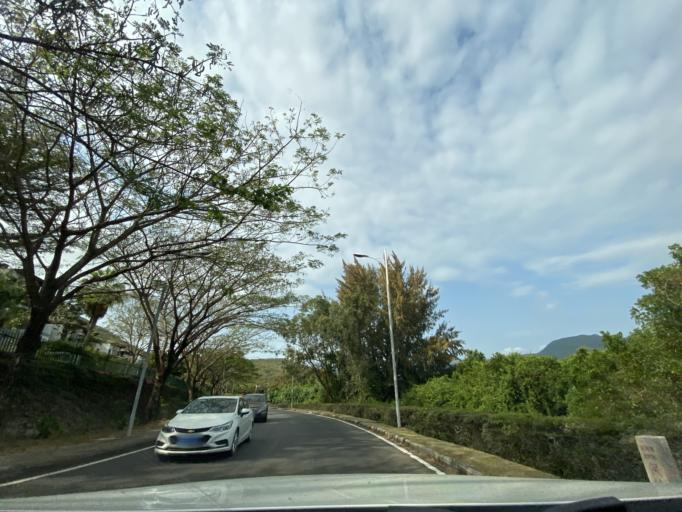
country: CN
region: Hainan
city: Tiandu
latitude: 18.2251
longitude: 109.6151
